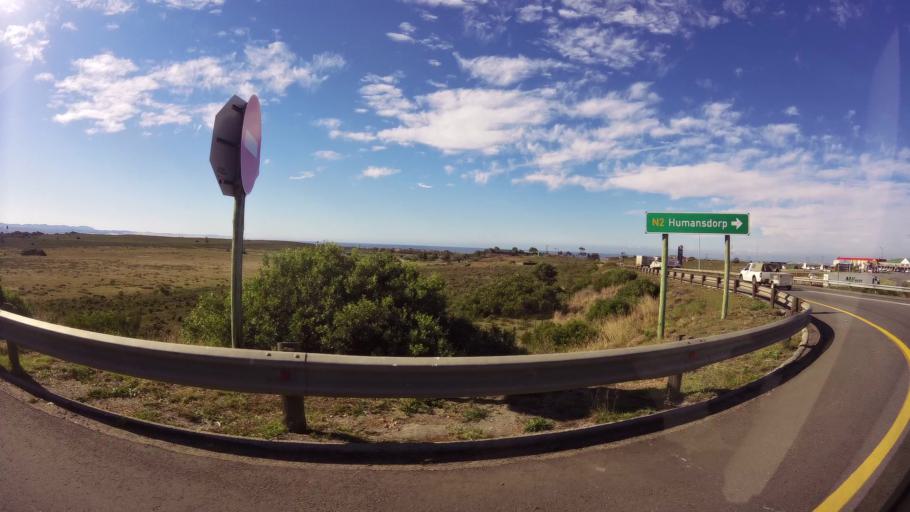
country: ZA
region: Eastern Cape
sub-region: Cacadu District Municipality
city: Jeffrey's Bay
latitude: -34.0142
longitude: 24.8855
